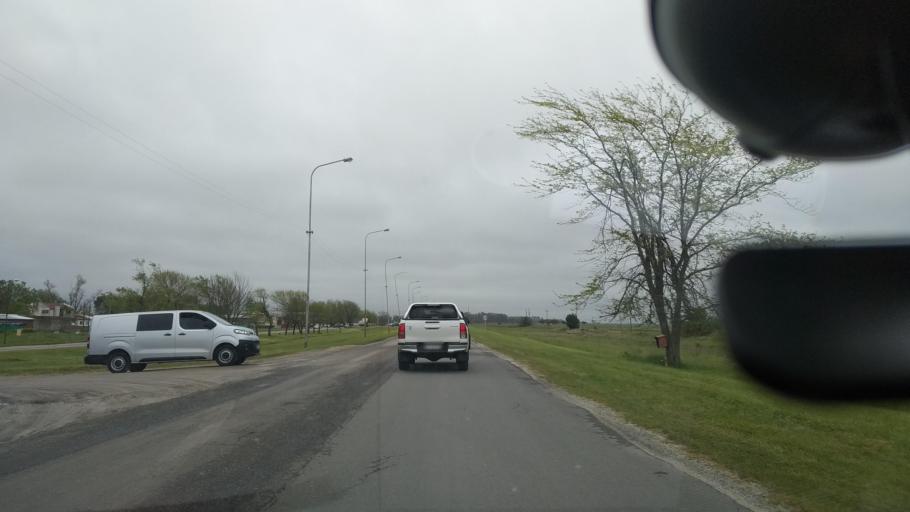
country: AR
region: Buenos Aires
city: Veronica
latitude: -35.5286
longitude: -57.3246
